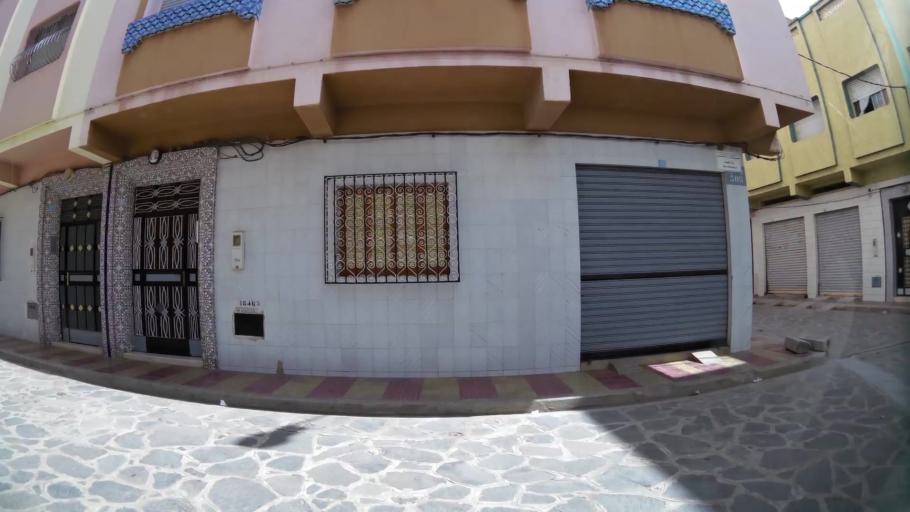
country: MA
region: Oriental
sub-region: Nador
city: Nador
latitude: 35.1620
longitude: -2.9301
